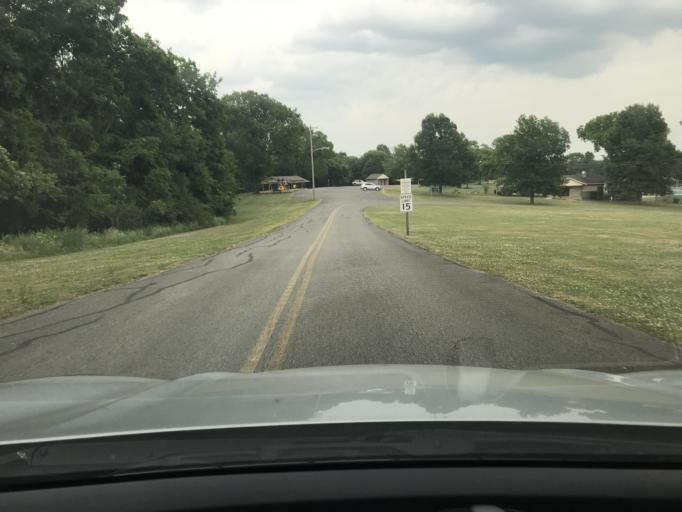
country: US
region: Tennessee
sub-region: Davidson County
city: Goodlettsville
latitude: 36.3061
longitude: -86.7107
